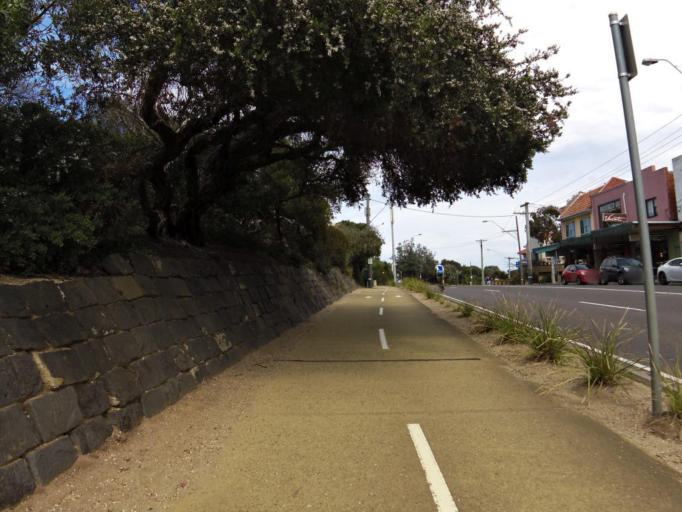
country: AU
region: Victoria
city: Beaumaris
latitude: -37.9917
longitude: 145.0423
